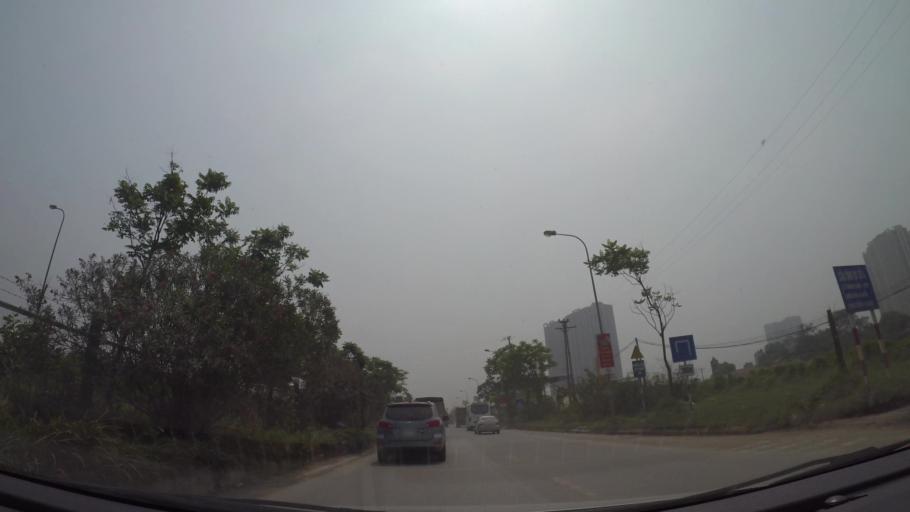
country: VN
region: Ha Noi
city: Cau Dien
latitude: 21.0104
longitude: 105.7253
